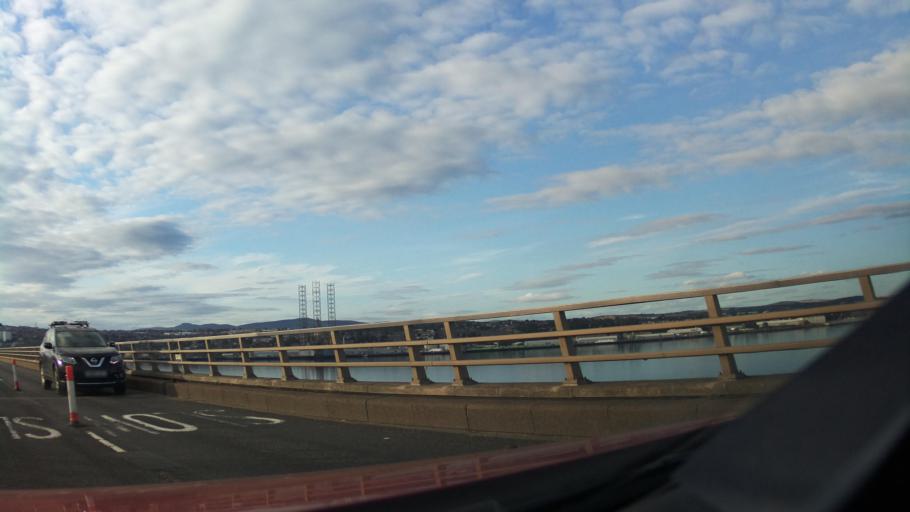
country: GB
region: Scotland
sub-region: Fife
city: Newport-On-Tay
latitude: 56.4489
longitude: -2.9379
